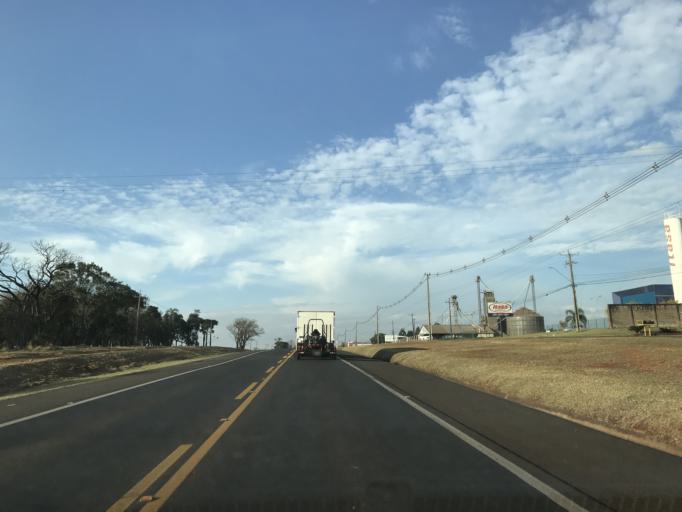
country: BR
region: Parana
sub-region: Cascavel
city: Cascavel
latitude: -25.0390
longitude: -53.5980
